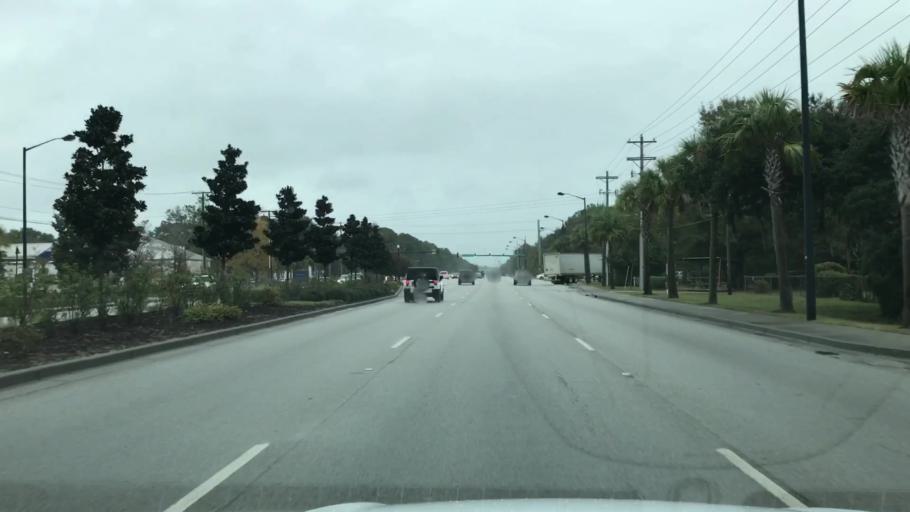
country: US
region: South Carolina
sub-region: Charleston County
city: Isle of Palms
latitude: 32.8606
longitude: -79.7927
